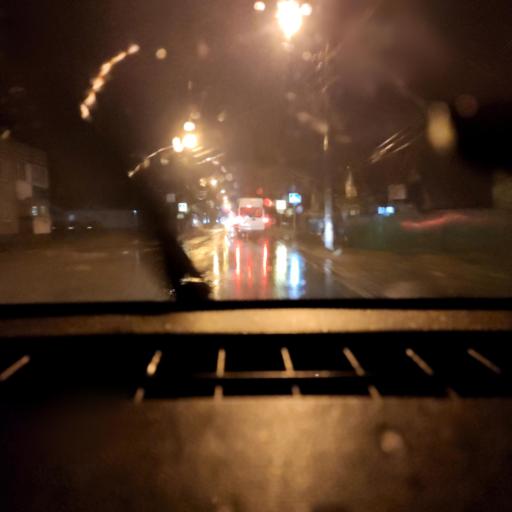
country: RU
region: Bashkortostan
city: Ufa
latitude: 54.8207
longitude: 56.1735
